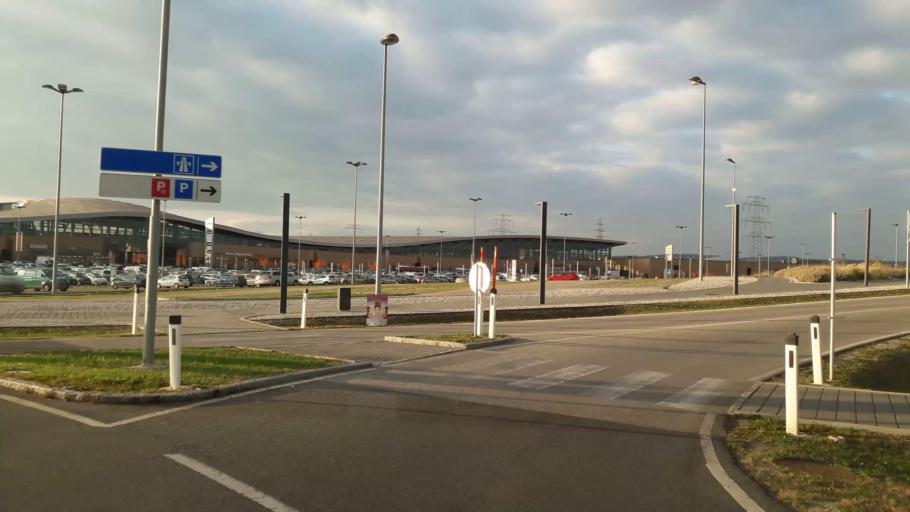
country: AT
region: Lower Austria
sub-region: Politischer Bezirk Mistelbach
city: Grossebersdorf
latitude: 48.3421
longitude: 16.4654
